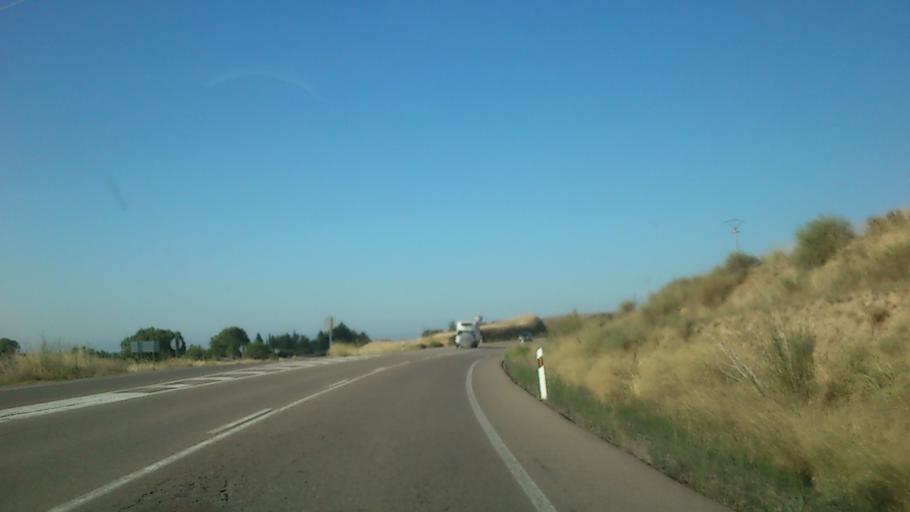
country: ES
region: Aragon
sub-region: Provincia de Zaragoza
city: Villanueva de Gallego
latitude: 41.7831
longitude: -0.8159
